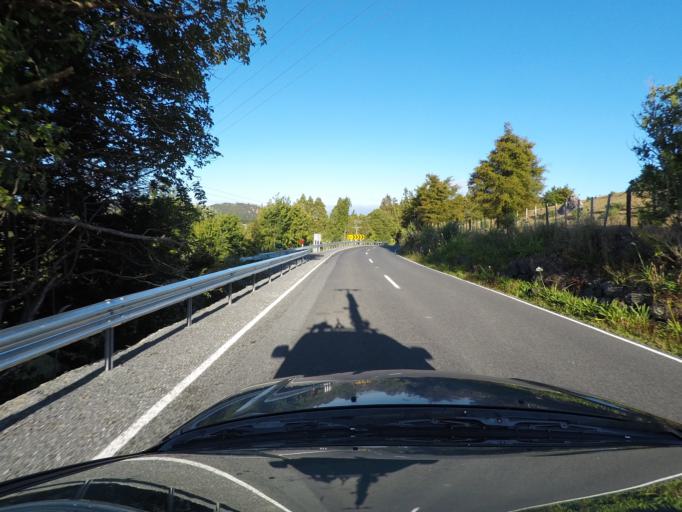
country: NZ
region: Northland
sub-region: Whangarei
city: Whangarei
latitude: -35.6560
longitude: 174.3112
